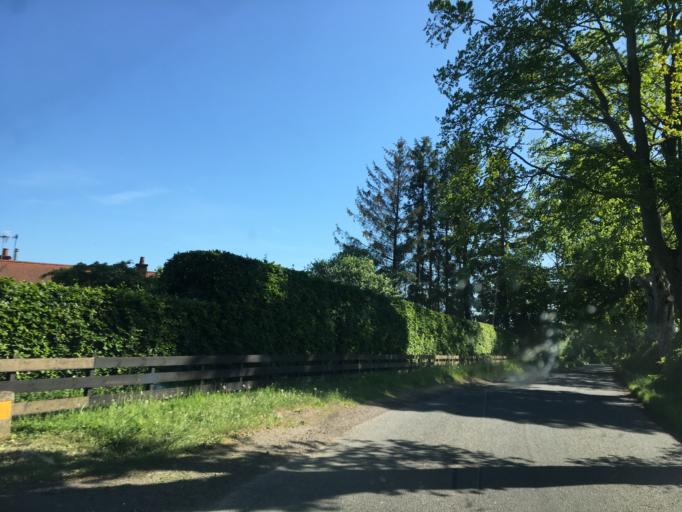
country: GB
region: Scotland
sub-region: Perth and Kinross
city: Methven
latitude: 56.4060
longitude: -3.5409
